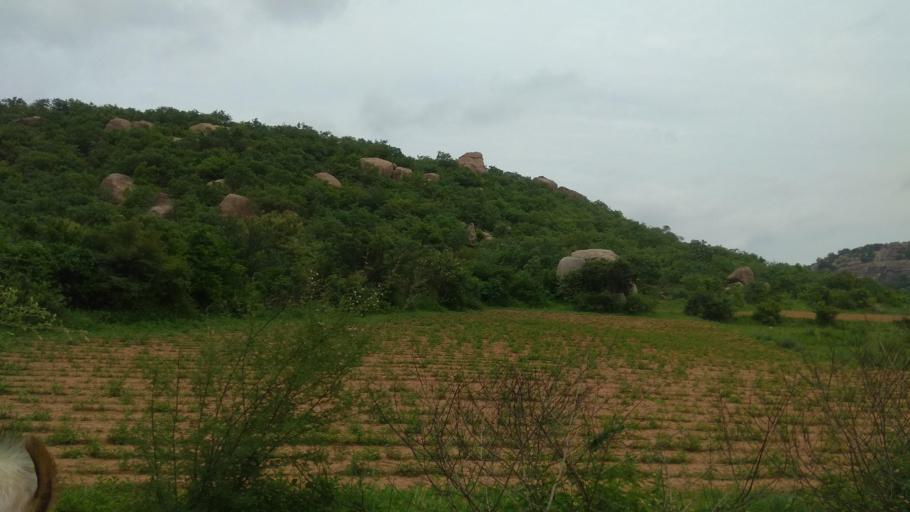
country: IN
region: Telangana
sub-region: Mahbubnagar
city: Farrukhnagar
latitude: 16.8833
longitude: 78.4986
